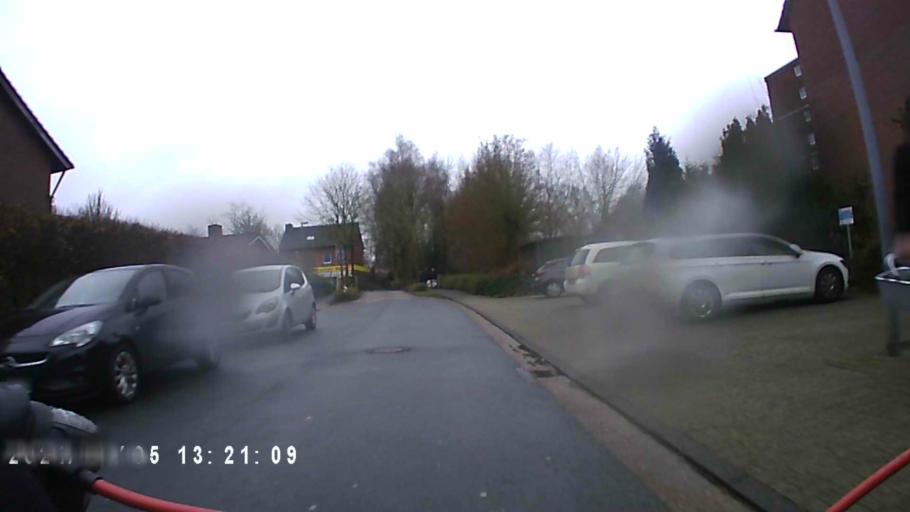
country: DE
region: Lower Saxony
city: Leer
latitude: 53.2330
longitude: 7.4385
